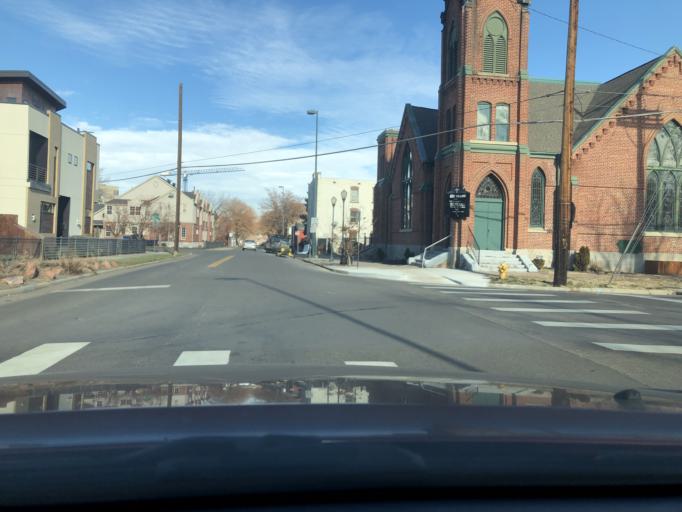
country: US
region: Colorado
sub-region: Denver County
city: Denver
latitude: 39.7506
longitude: -104.9781
